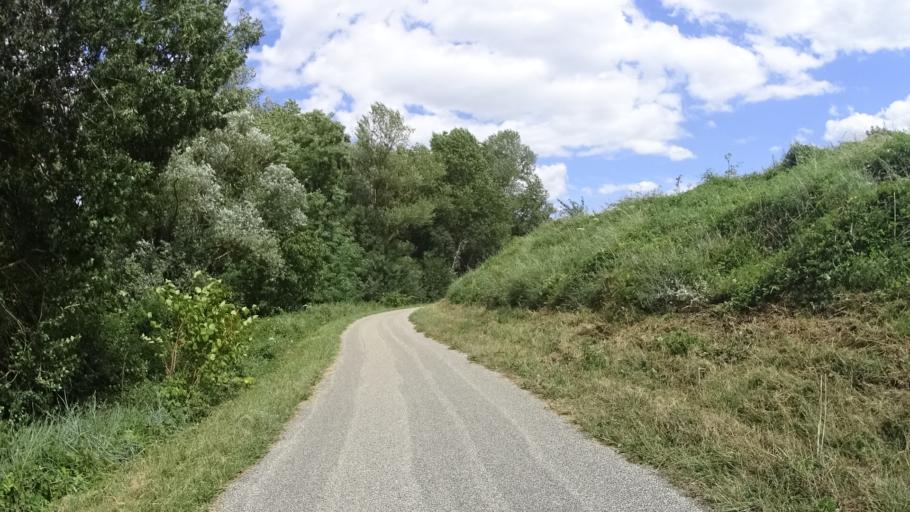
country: FR
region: Centre
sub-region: Departement d'Indre-et-Loire
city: La Ville-aux-Dames
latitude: 47.4041
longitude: 0.7601
